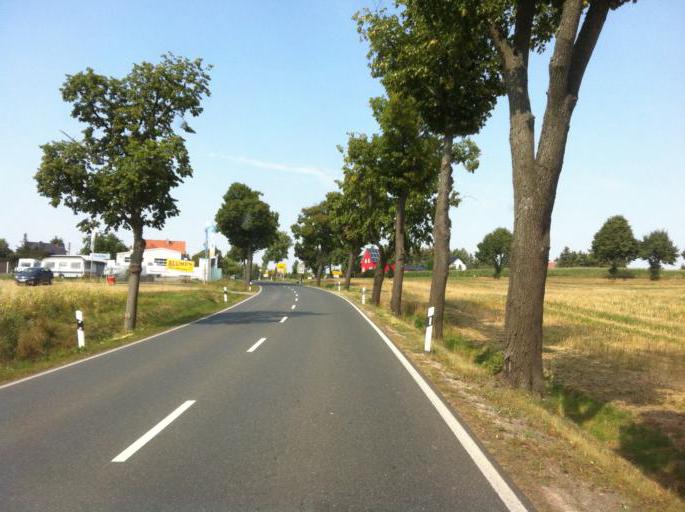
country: DE
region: Saxony
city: Neumark
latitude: 50.6722
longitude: 12.3950
